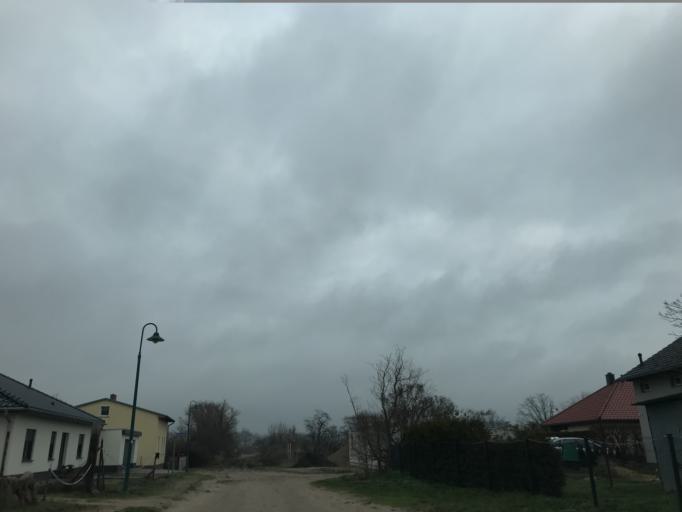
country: DE
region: Brandenburg
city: Wustermark
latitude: 52.5919
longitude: 12.9289
